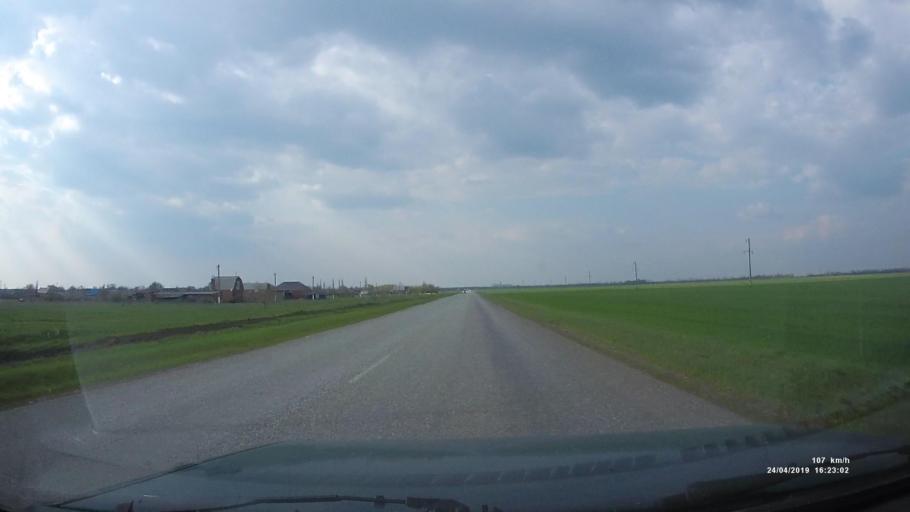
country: RU
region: Rostov
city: Orlovskiy
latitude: 46.8286
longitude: 42.0519
